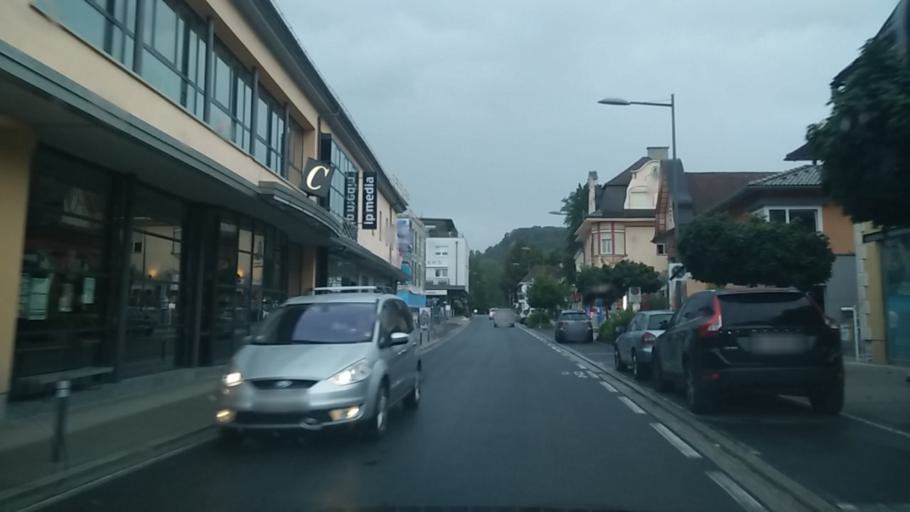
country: AT
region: Carinthia
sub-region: Politischer Bezirk Klagenfurt Land
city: Maria Worth
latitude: 46.6363
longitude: 14.1403
